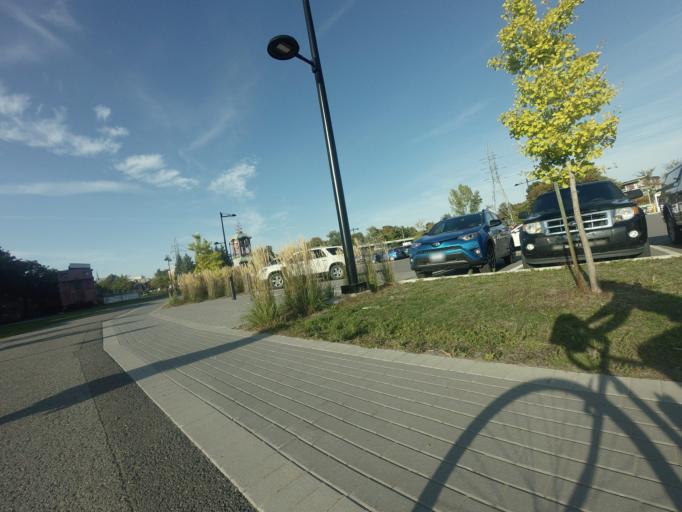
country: CA
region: Quebec
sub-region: Laurentides
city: Saint-Jerome
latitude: 45.7754
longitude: -74.0001
